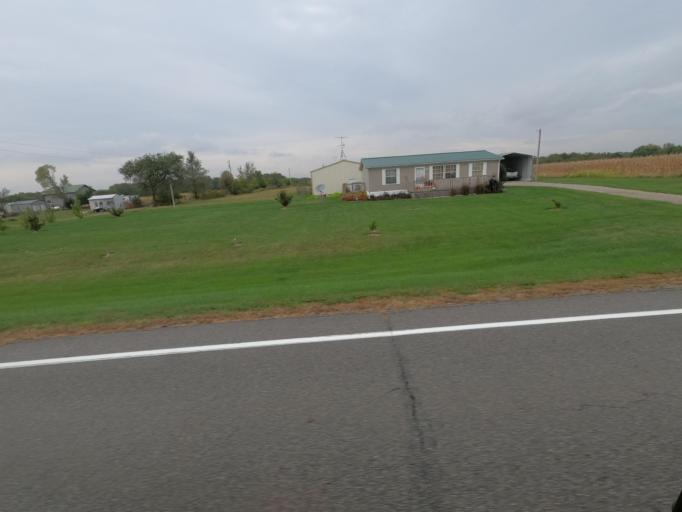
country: US
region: Iowa
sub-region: Van Buren County
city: Keosauqua
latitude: 40.8093
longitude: -91.9204
